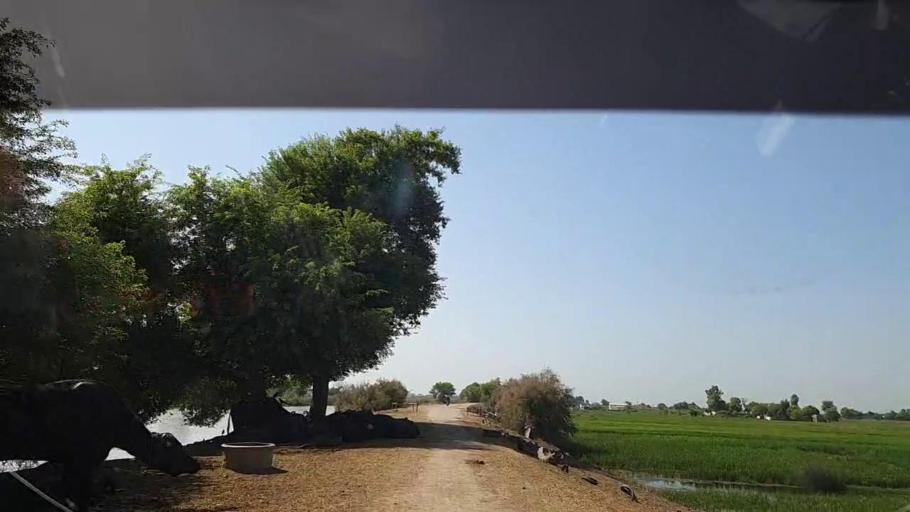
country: PK
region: Sindh
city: Ghauspur
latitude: 28.1947
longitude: 69.0502
